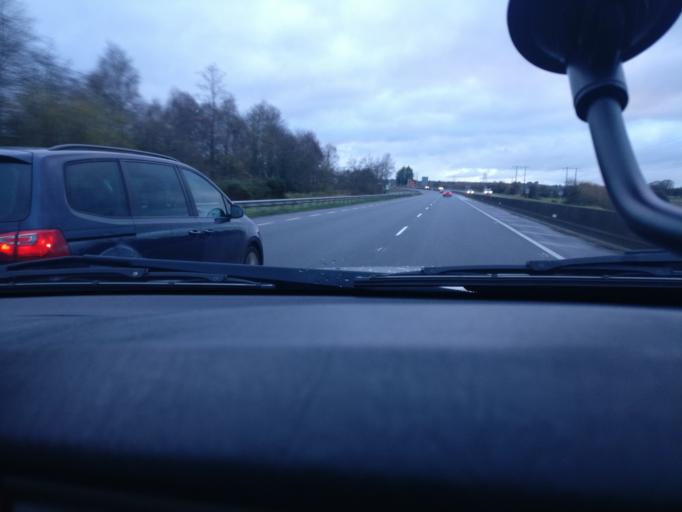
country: IE
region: Leinster
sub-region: An Iarmhi
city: Athlone
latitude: 53.4349
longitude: -7.9469
